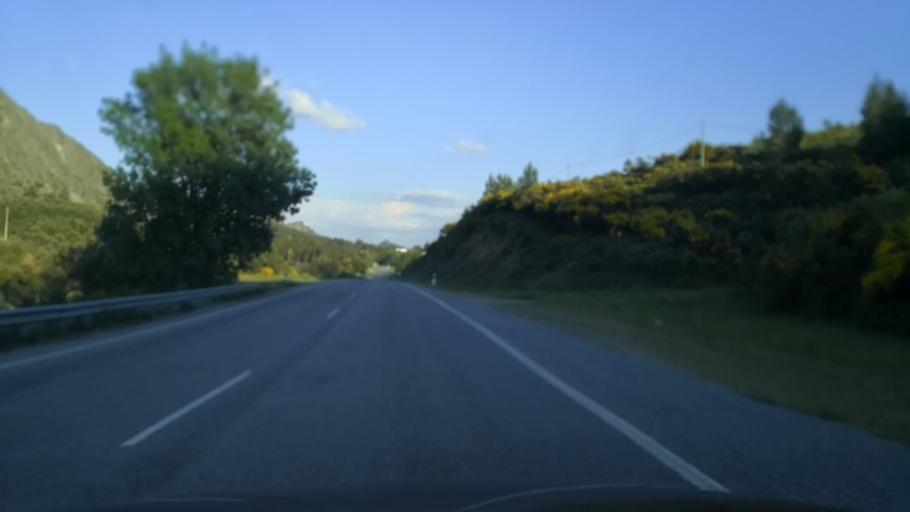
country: PT
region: Portalegre
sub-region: Portalegre
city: Sao Juliao
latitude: 39.3588
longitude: -7.3186
